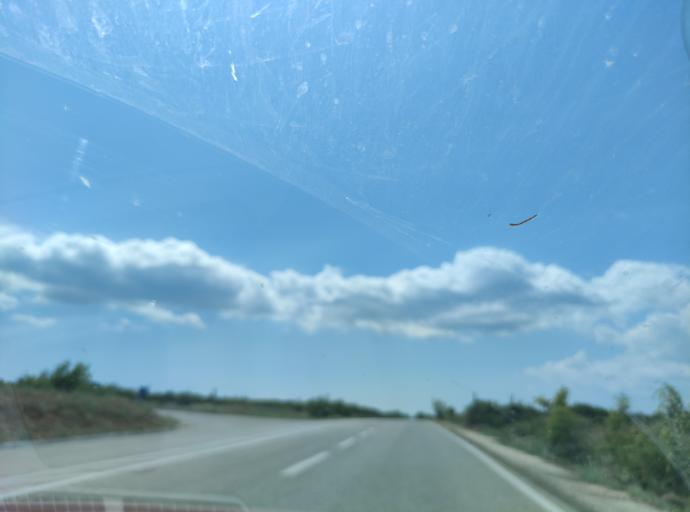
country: GR
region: East Macedonia and Thrace
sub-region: Nomos Dramas
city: Fotolivos
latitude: 40.9913
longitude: 24.0742
